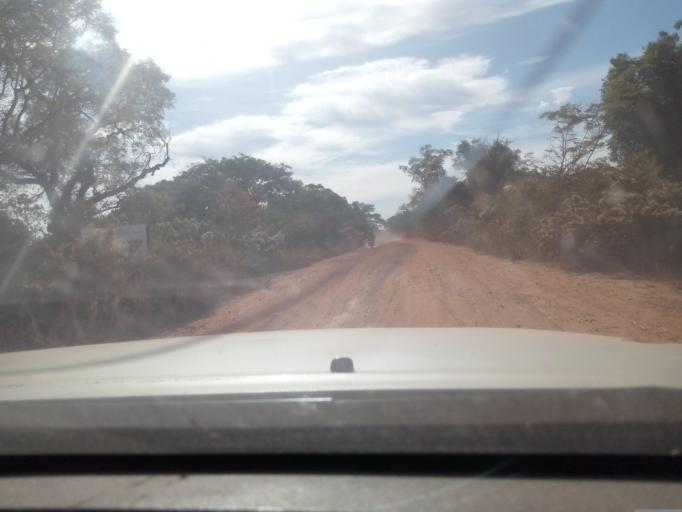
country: ML
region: Sikasso
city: Sikasso
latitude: 11.8910
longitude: -6.0476
